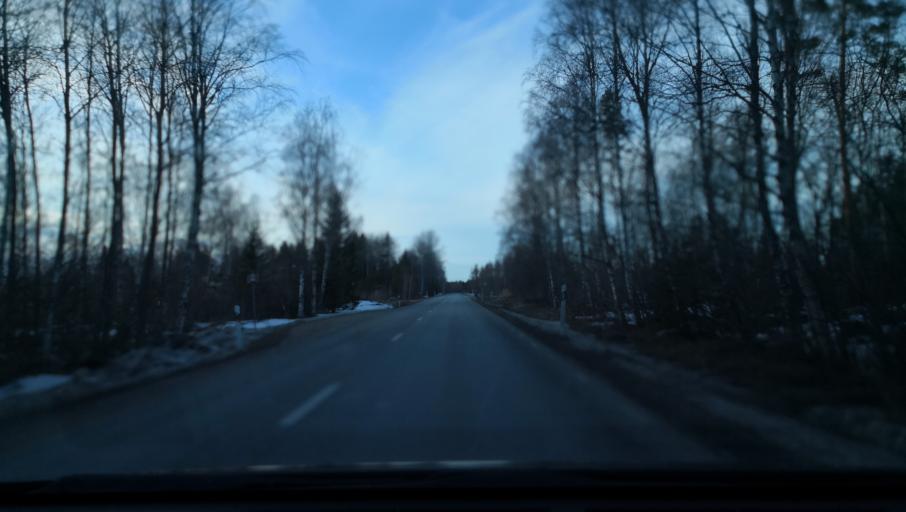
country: SE
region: Uppsala
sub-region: Osthammars Kommun
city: OEsthammar
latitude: 60.3245
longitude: 18.2498
